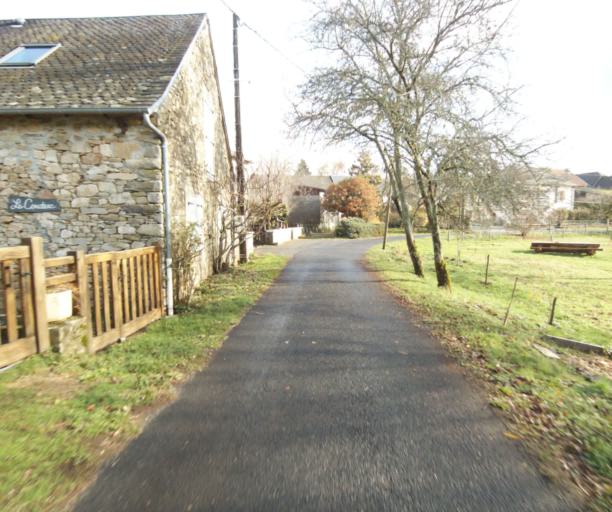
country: FR
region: Limousin
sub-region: Departement de la Correze
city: Cornil
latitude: 45.2248
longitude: 1.6873
